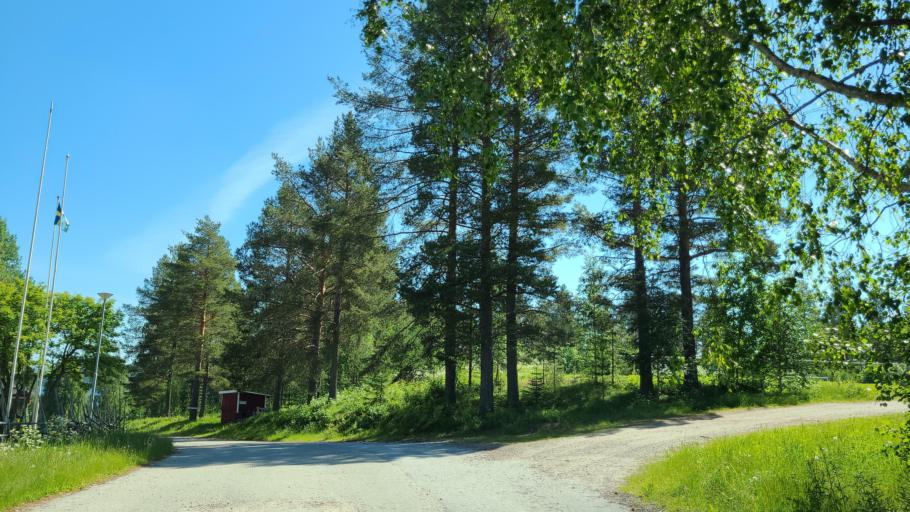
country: SE
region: Vaesterbotten
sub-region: Bjurholms Kommun
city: Bjurholm
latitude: 63.6901
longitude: 18.8644
